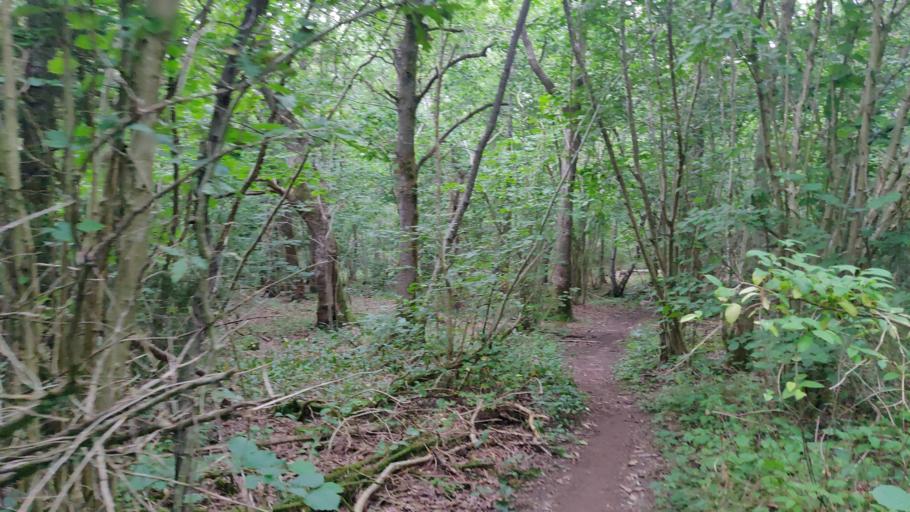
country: SE
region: Vaestra Goetaland
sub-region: Goteborg
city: Torslanda
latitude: 57.7839
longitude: 11.8205
